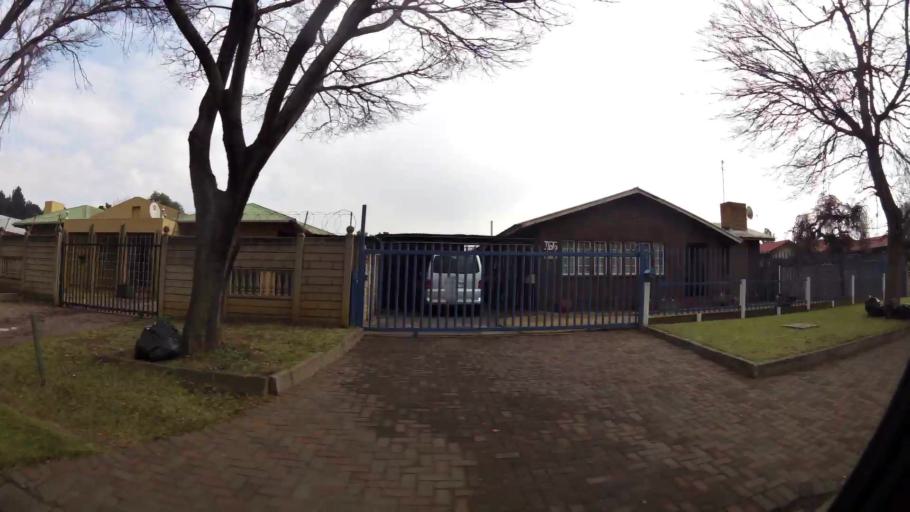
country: ZA
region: Gauteng
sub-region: Sedibeng District Municipality
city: Vanderbijlpark
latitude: -26.6861
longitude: 27.8282
